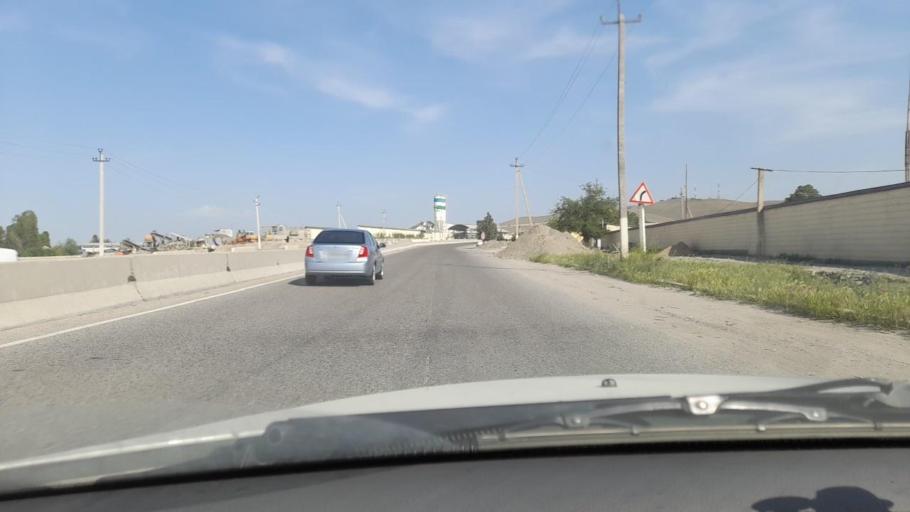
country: UZ
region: Samarqand
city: Samarqand
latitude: 39.7003
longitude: 67.0157
